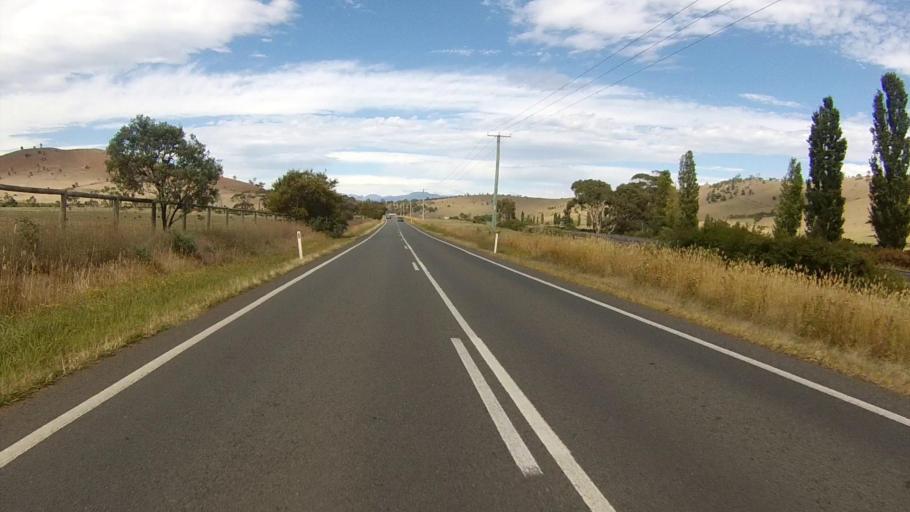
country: AU
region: Tasmania
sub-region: Brighton
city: Old Beach
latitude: -42.6726
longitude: 147.3613
